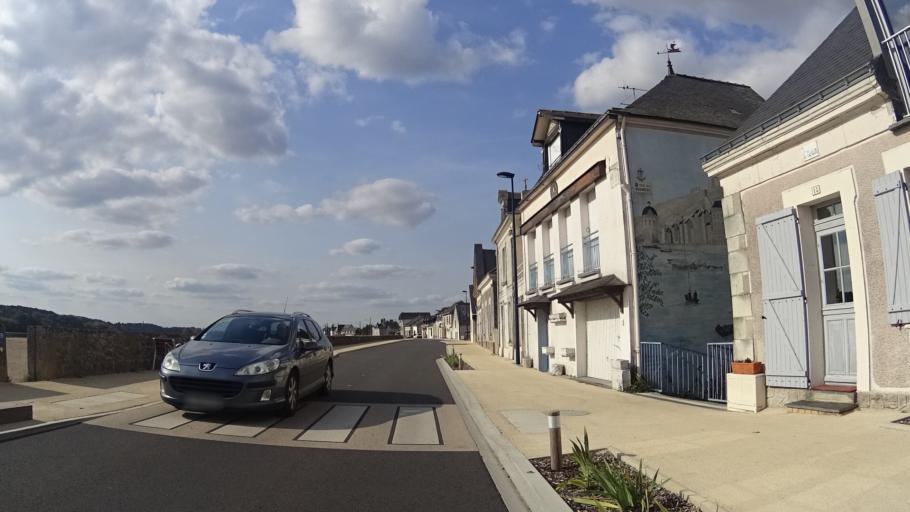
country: FR
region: Pays de la Loire
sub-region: Departement de Maine-et-Loire
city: Saint-Clement-des-Levees
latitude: 47.3311
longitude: -0.1863
